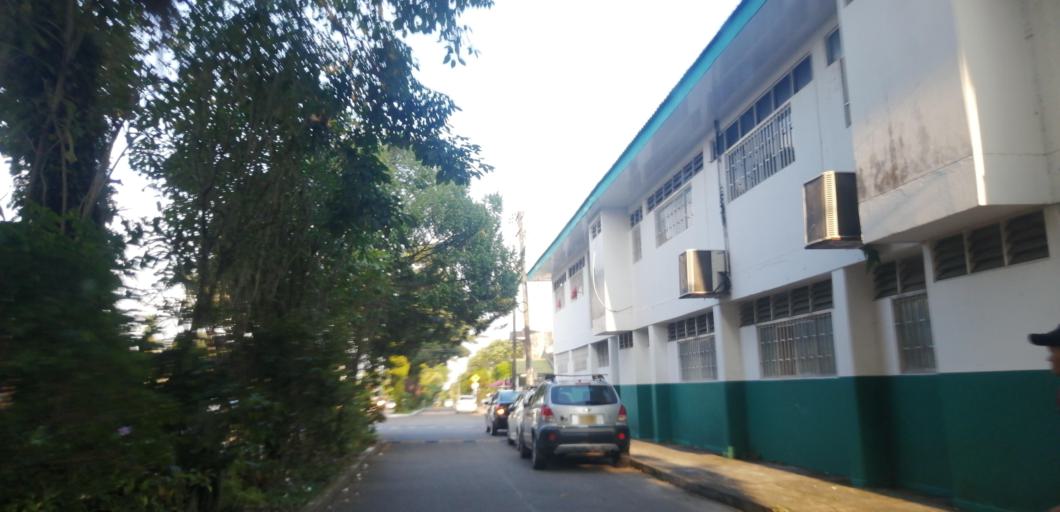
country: CO
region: Meta
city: Acacias
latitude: 3.9831
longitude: -73.7620
